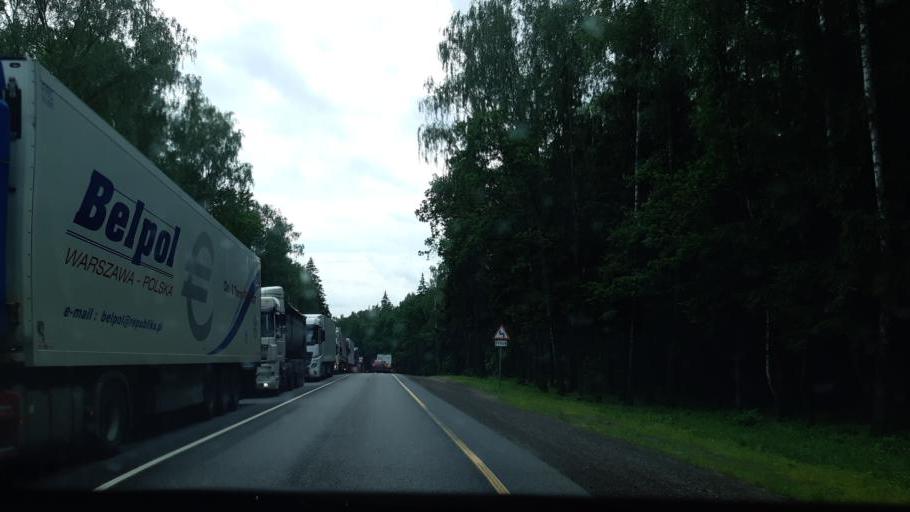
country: RU
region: Moskovskaya
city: Dorokhovo
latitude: 55.5251
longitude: 36.3547
